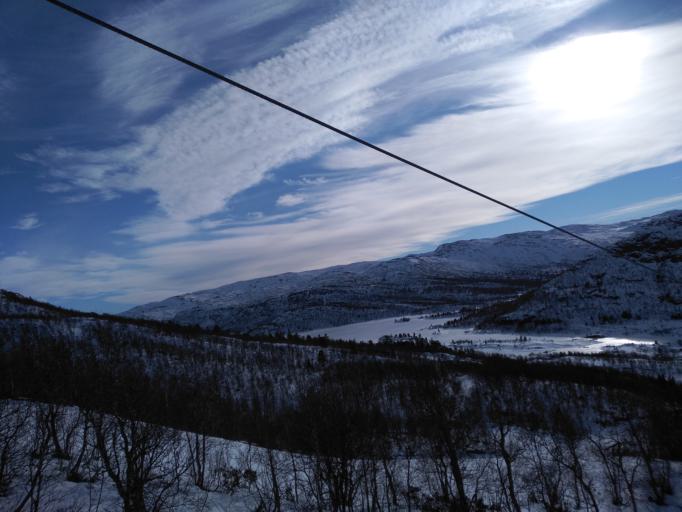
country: NO
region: Aust-Agder
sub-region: Bykle
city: Hovden
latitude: 59.5730
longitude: 7.3082
